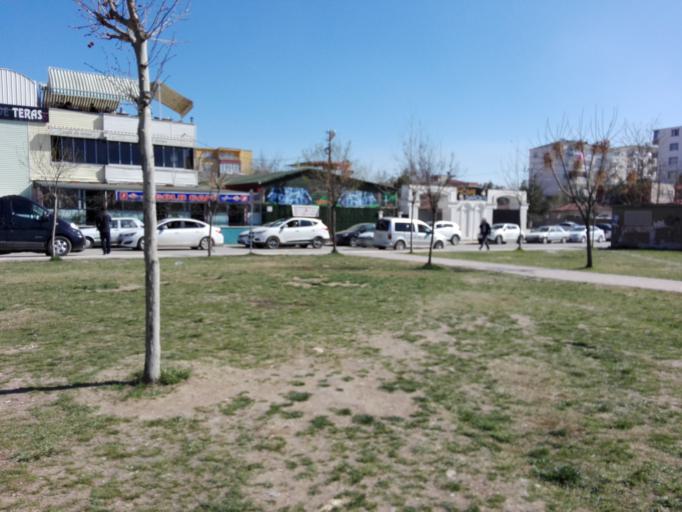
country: TR
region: Batman
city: Batman
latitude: 37.8949
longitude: 41.1331
